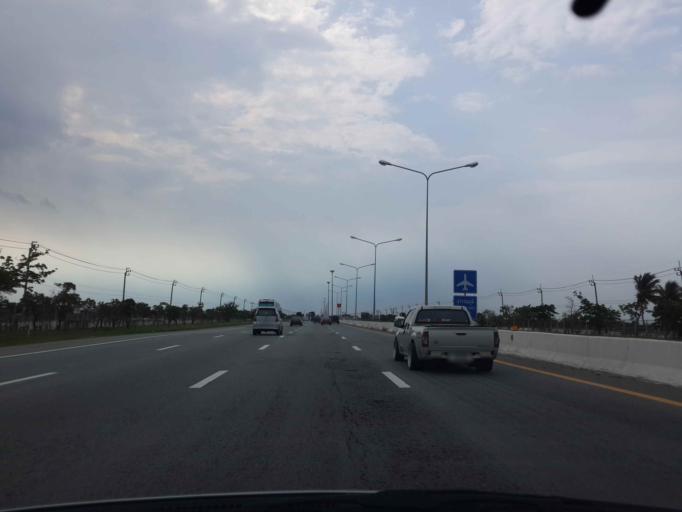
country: TH
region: Samut Prakan
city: Ban Khlong Bang Sao Thong
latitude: 13.6380
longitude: 100.8936
